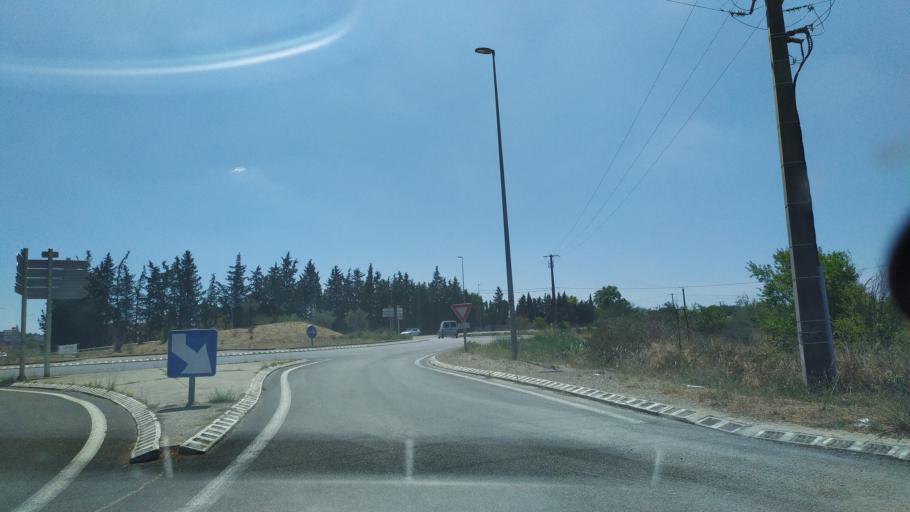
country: FR
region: Languedoc-Roussillon
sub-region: Departement du Gard
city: Vauvert
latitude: 43.7118
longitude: 4.2649
